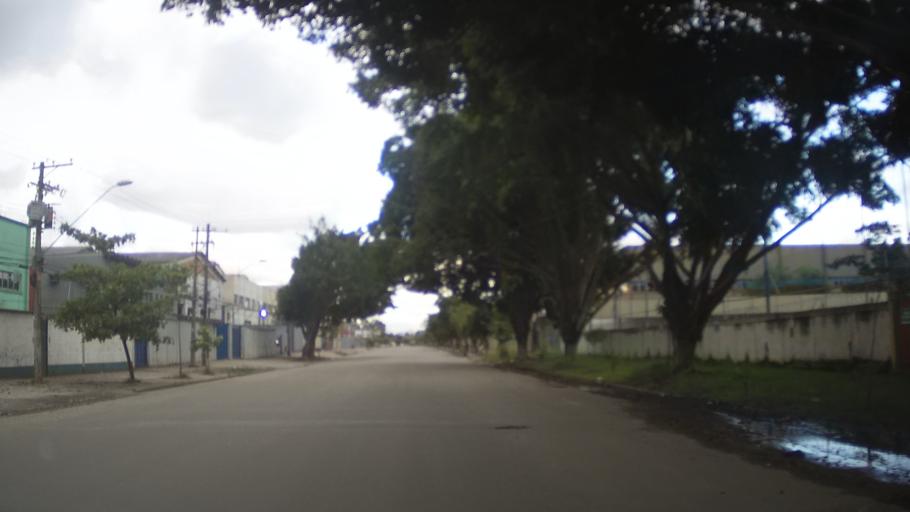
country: BR
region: Sao Paulo
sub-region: Guarulhos
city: Guarulhos
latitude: -23.4721
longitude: -46.4641
